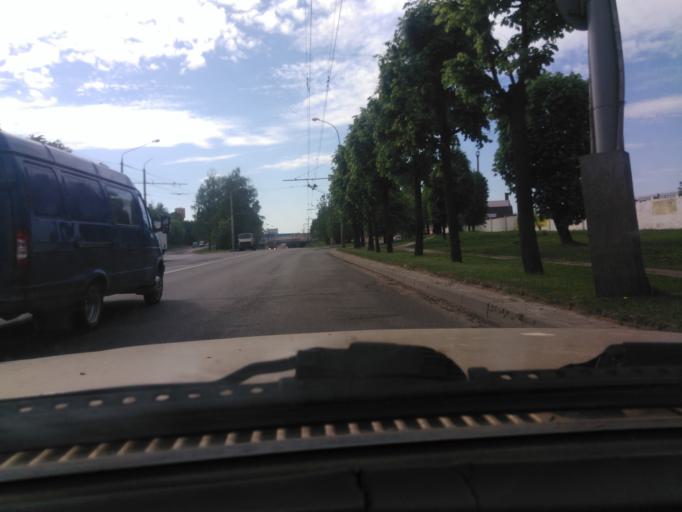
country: BY
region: Mogilev
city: Buynichy
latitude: 53.8946
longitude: 30.2973
